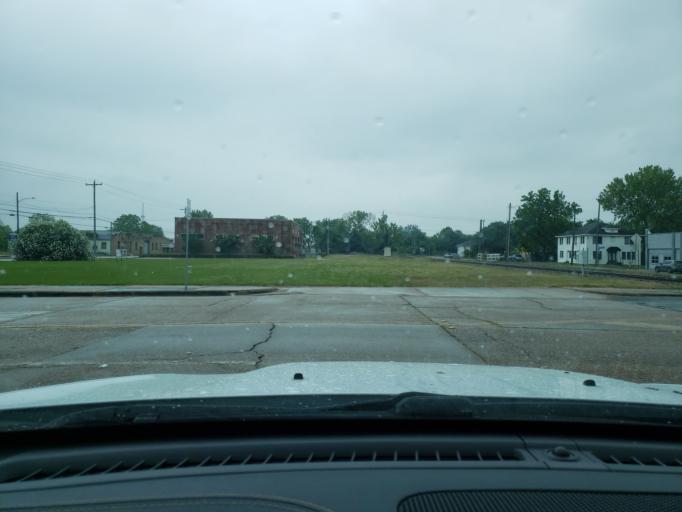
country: US
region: Texas
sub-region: Harris County
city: Baytown
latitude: 29.7324
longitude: -94.9682
